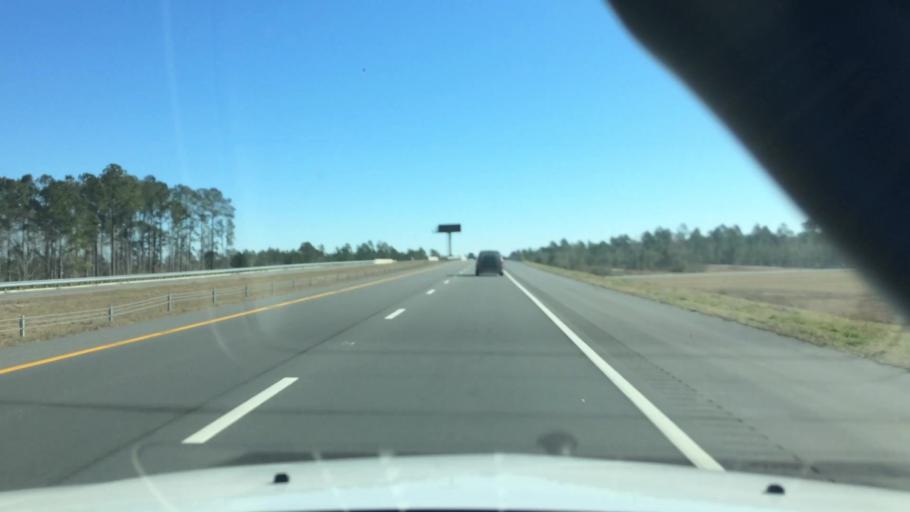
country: US
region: North Carolina
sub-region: Brunswick County
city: Navassa
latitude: 34.2729
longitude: -78.0205
